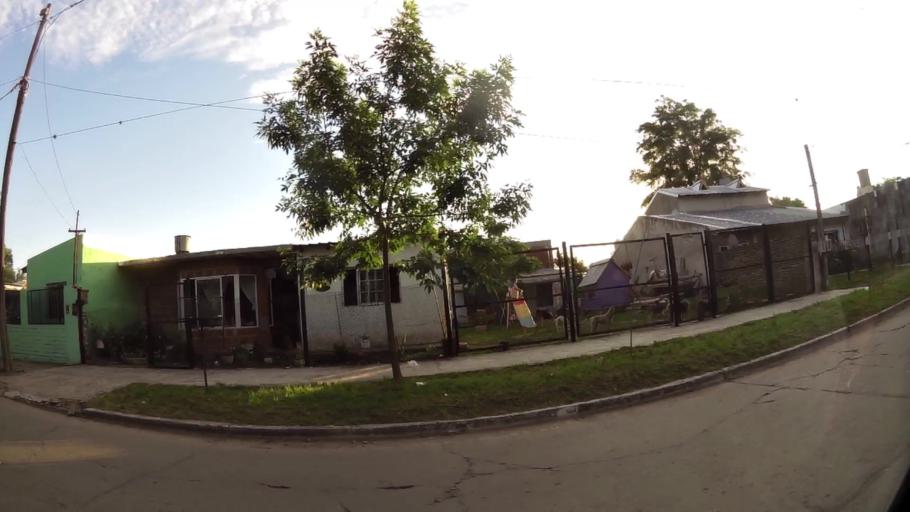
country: AR
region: Buenos Aires
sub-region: Partido de Merlo
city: Merlo
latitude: -34.6779
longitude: -58.7619
